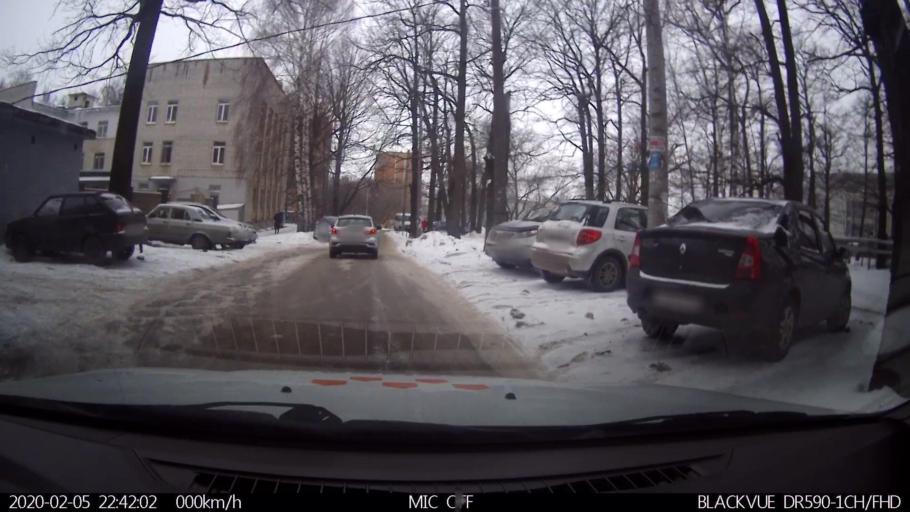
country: RU
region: Nizjnij Novgorod
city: Imeni Stepana Razina
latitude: 54.7191
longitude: 44.3488
